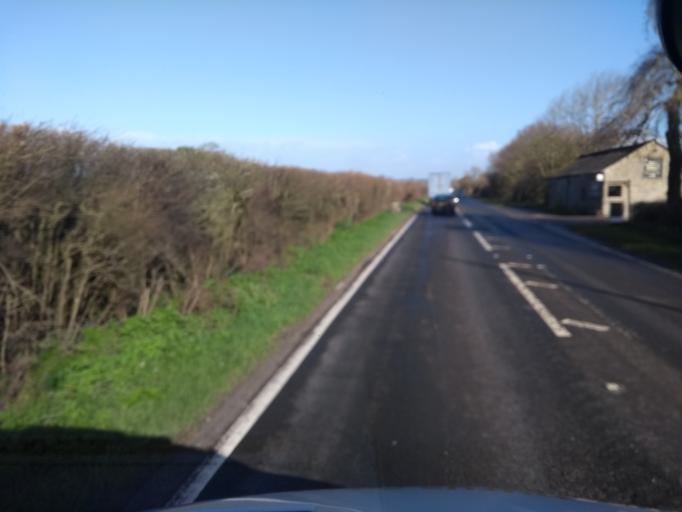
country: GB
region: England
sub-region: Somerset
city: Ilchester
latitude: 50.9860
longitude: -2.6766
